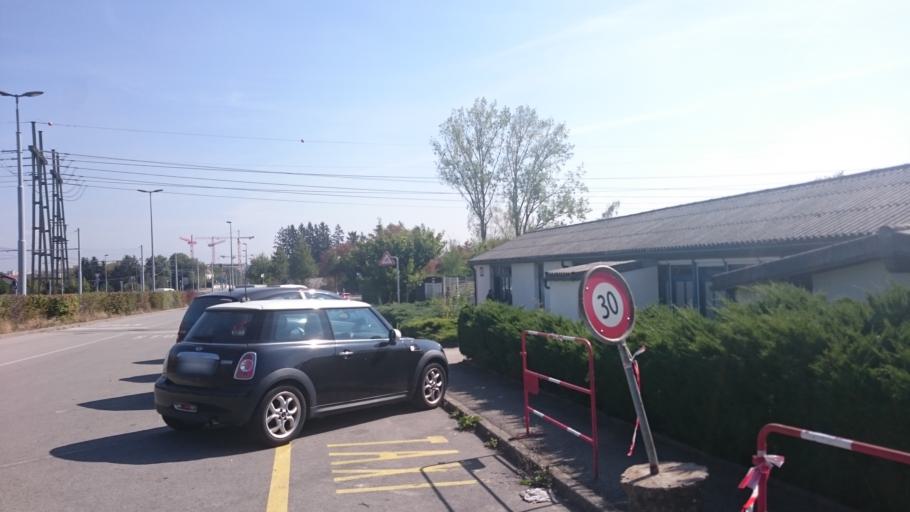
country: CH
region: Geneva
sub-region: Geneva
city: Meyrin
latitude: 46.2330
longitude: 6.0563
